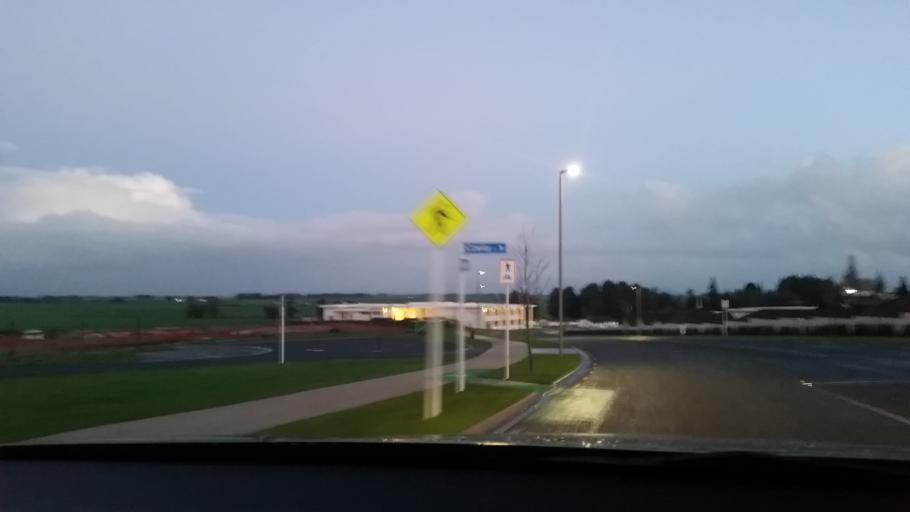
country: NZ
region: Waikato
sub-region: Hamilton City
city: Hamilton
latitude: -37.8190
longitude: 175.2263
